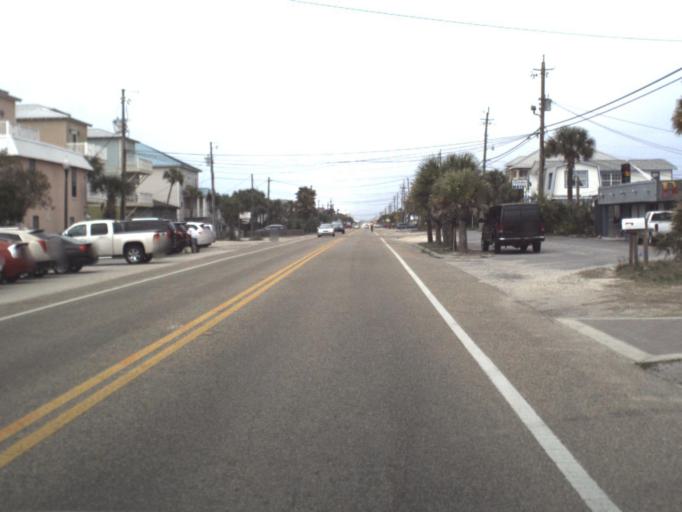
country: US
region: Florida
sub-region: Bay County
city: Laguna Beach
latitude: 30.2428
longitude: -85.9316
